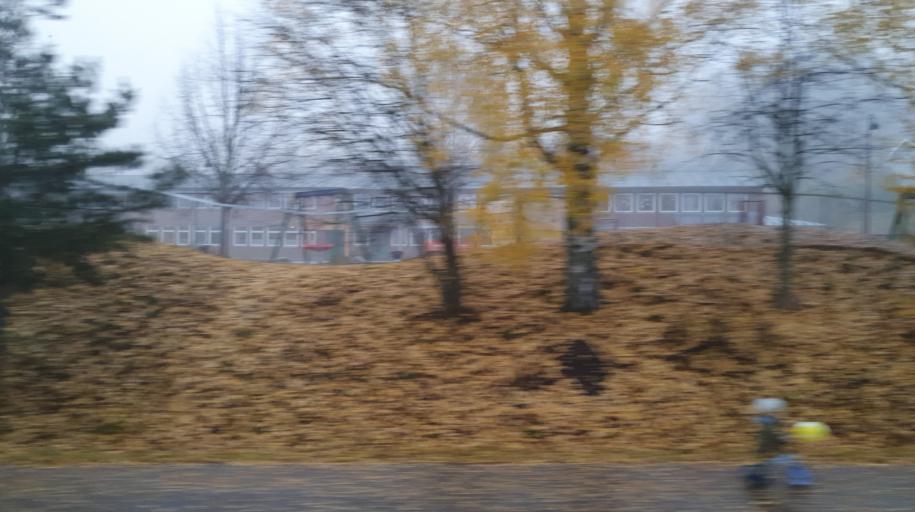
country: NO
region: Buskerud
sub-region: Modum
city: Vikersund
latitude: 59.8917
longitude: 9.9263
